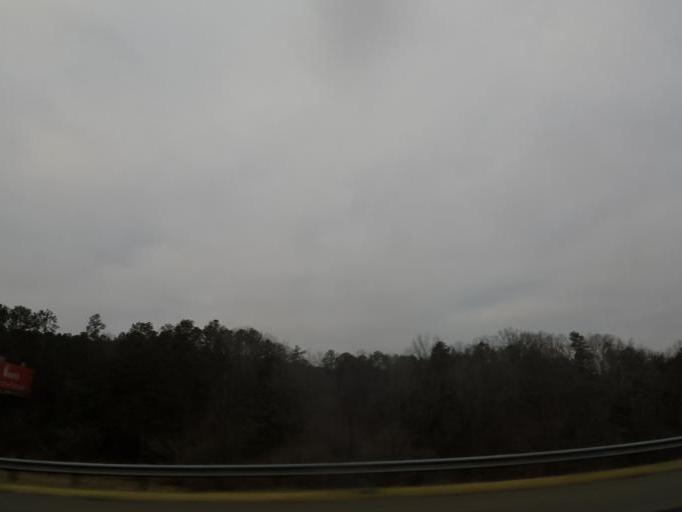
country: US
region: Alabama
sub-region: Jefferson County
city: Kimberly
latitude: 33.7617
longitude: -86.8310
